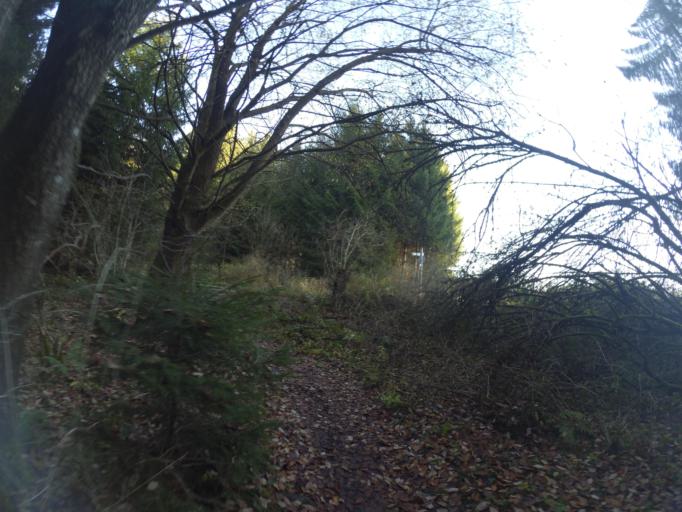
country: DE
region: Bavaria
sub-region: Swabia
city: Ruderatshofen
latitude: 47.8017
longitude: 10.5591
